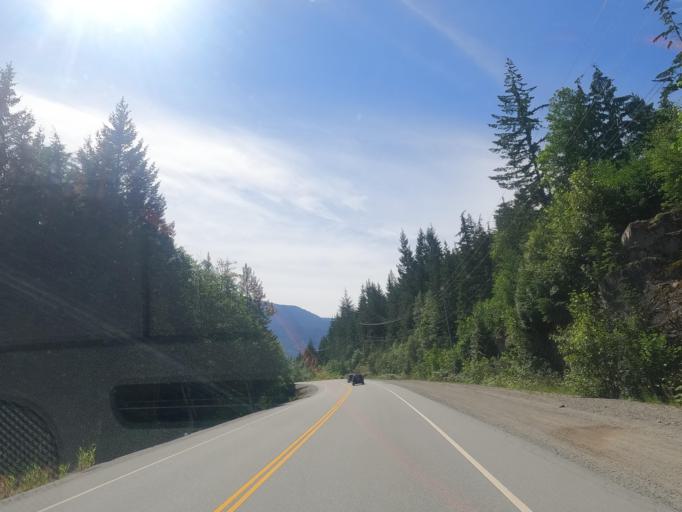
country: CA
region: British Columbia
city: Whistler
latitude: 50.1950
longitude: -122.8818
